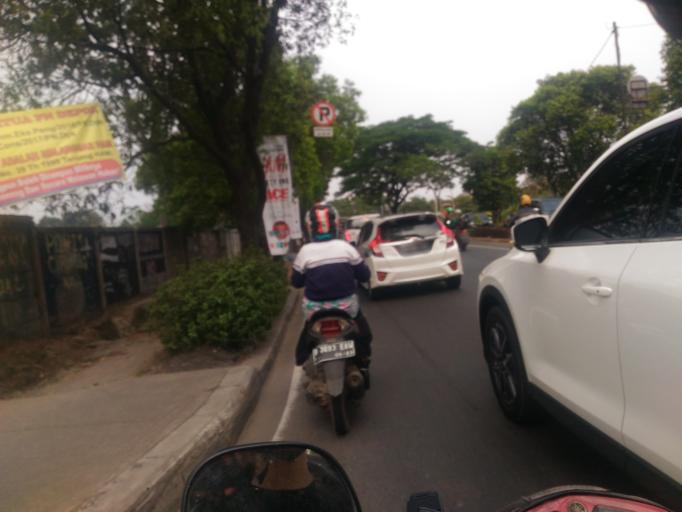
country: ID
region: West Java
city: Depok
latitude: -6.3791
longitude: 106.8478
